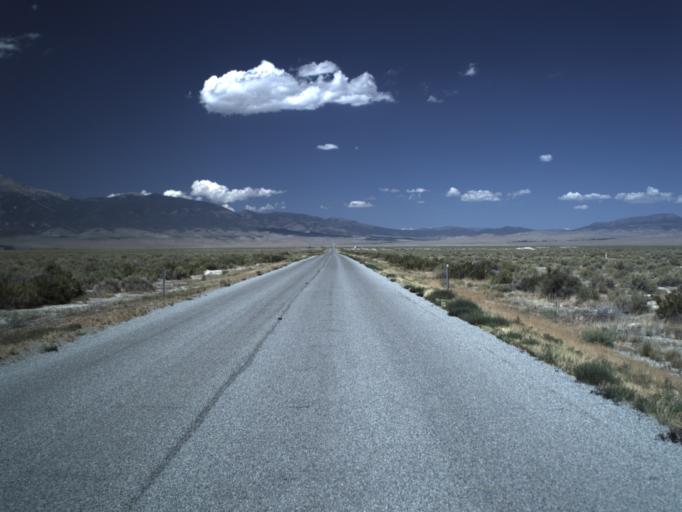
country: US
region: Nevada
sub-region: White Pine County
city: McGill
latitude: 39.0523
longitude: -113.9857
